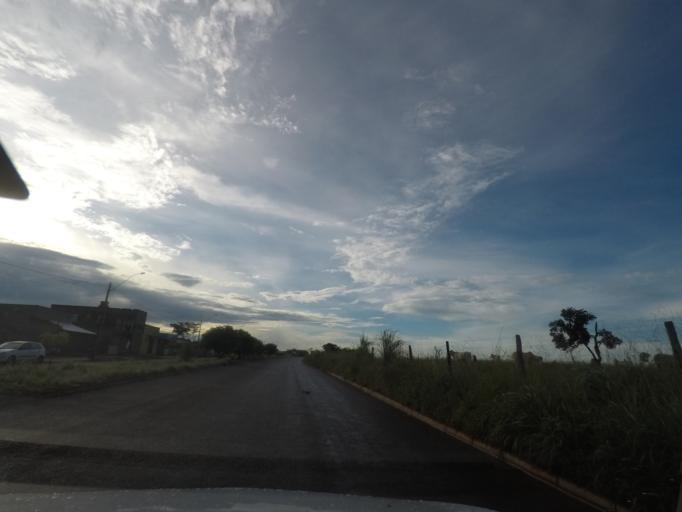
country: BR
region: Goias
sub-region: Trindade
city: Trindade
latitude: -16.7490
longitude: -49.3854
